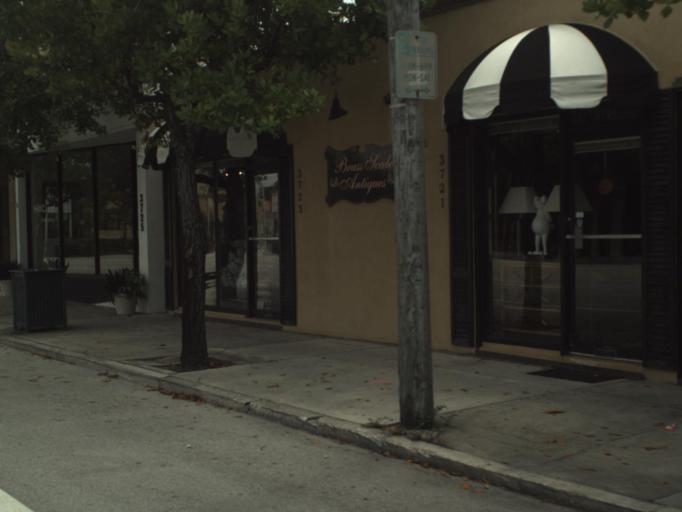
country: US
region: Florida
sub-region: Palm Beach County
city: Palm Beach
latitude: 26.6776
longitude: -80.0548
